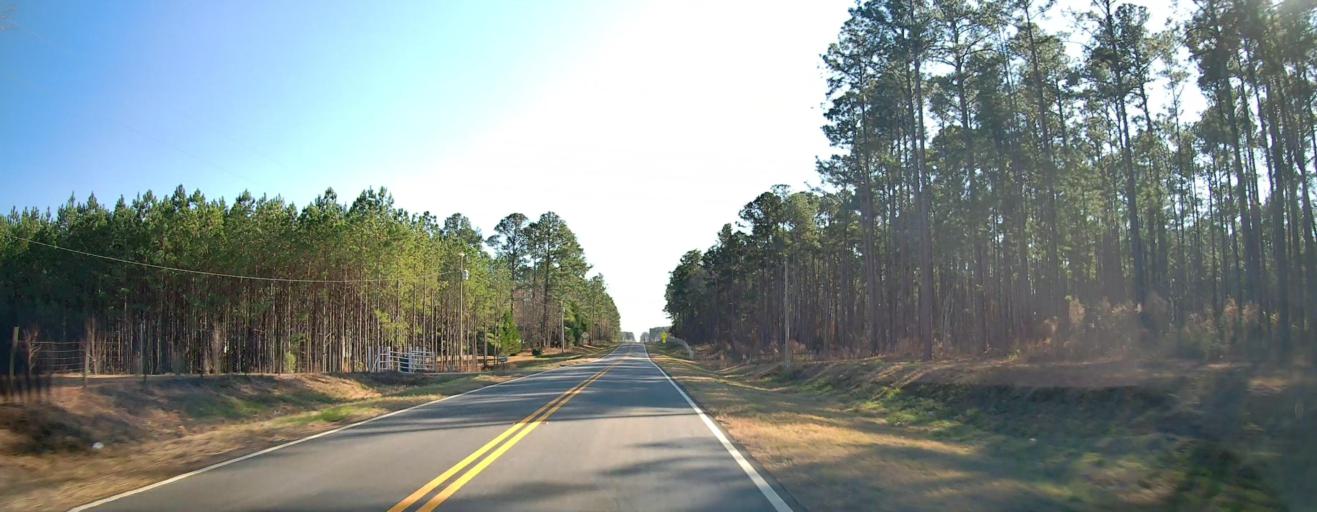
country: US
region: Georgia
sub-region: Sumter County
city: Americus
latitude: 32.0743
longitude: -84.1663
